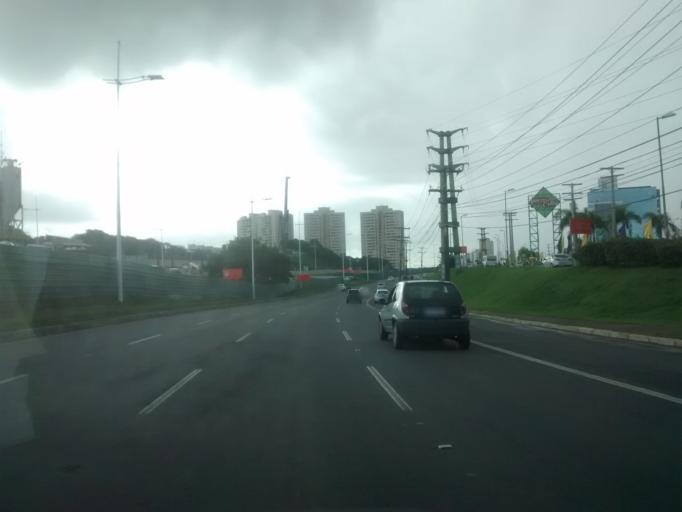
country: BR
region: Bahia
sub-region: Salvador
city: Salvador
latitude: -12.9409
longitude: -38.4174
